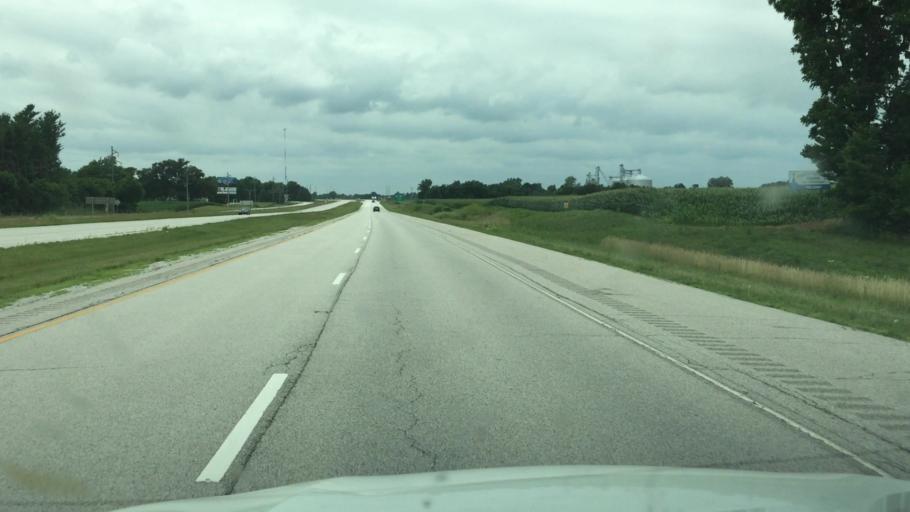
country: US
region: Illinois
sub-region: Hancock County
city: Carthage
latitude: 40.4161
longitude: -91.0915
